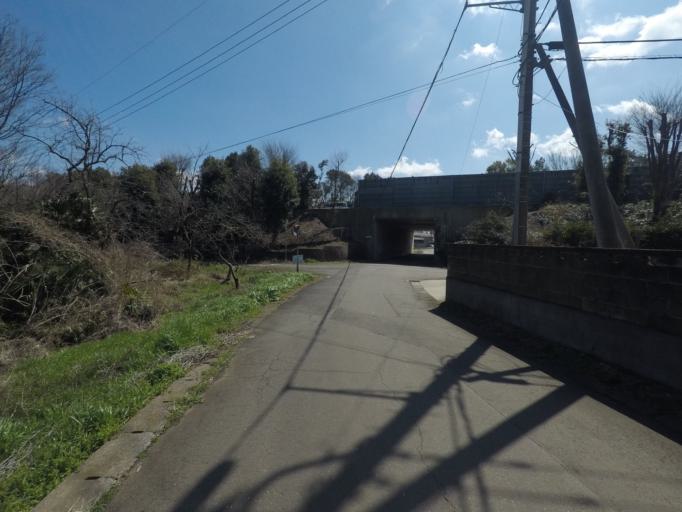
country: JP
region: Ibaraki
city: Ushiku
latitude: 36.0199
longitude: 140.0685
